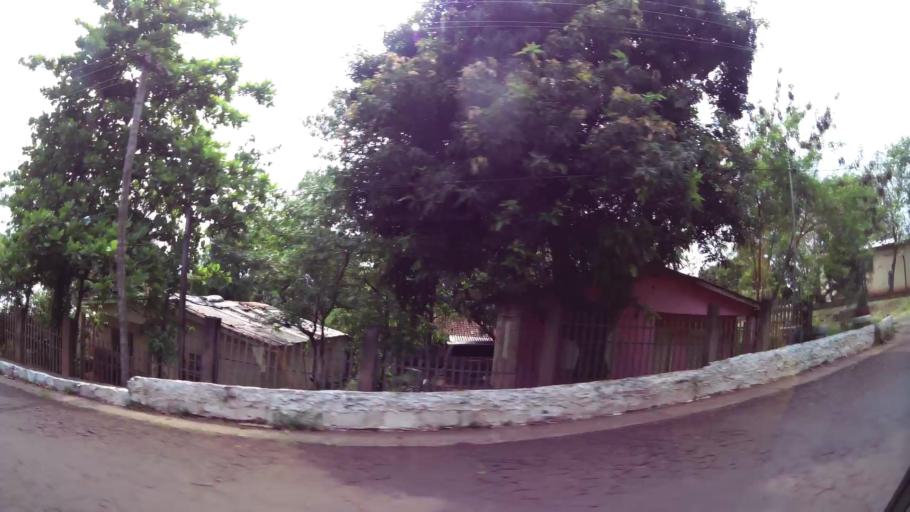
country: BR
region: Parana
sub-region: Foz Do Iguacu
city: Foz do Iguacu
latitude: -25.5539
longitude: -54.6023
